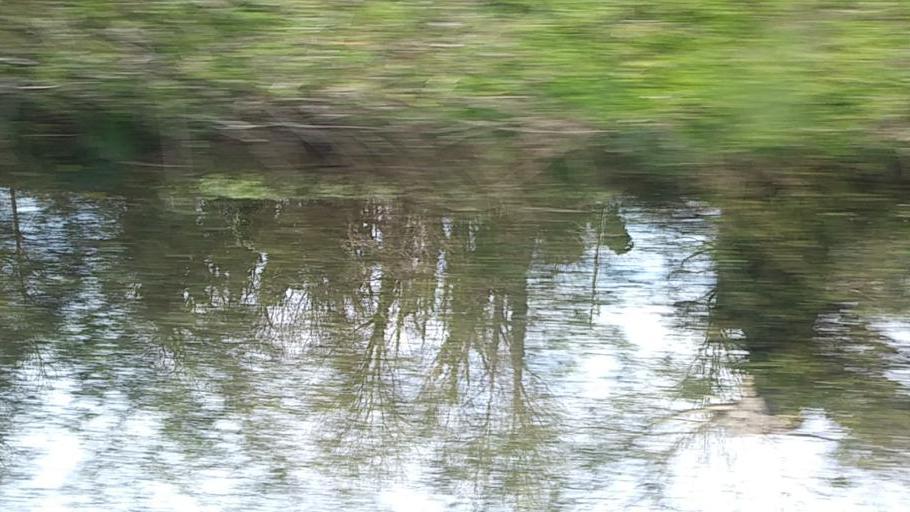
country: US
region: Tennessee
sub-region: Campbell County
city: Hunter
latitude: 36.3628
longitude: -84.1323
